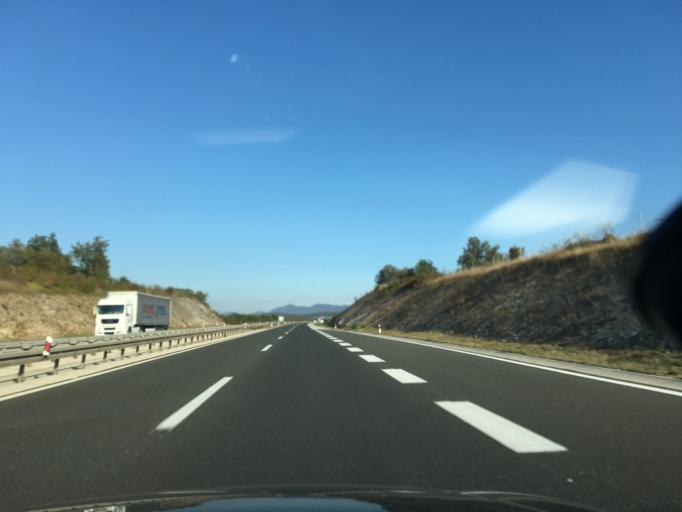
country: HR
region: Licko-Senjska
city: Gospic
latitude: 44.6719
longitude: 15.4176
